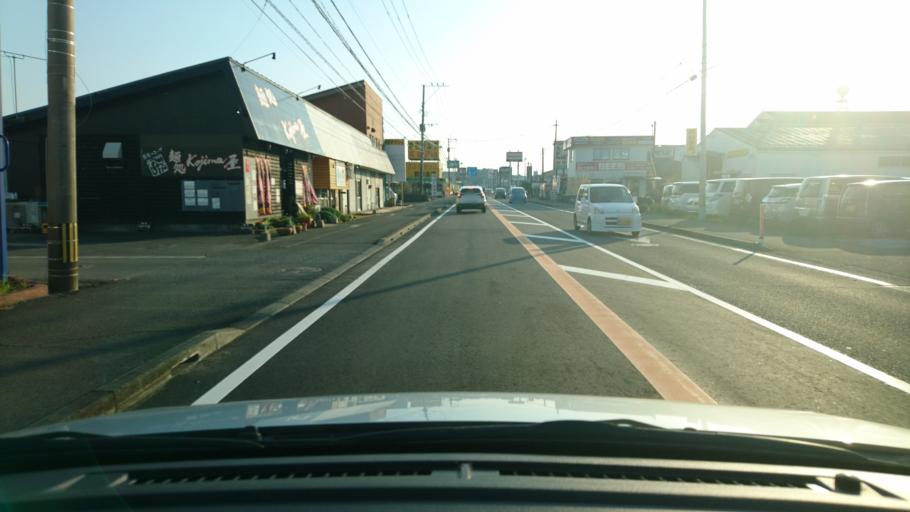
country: JP
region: Miyazaki
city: Miyazaki-shi
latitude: 31.9794
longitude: 131.4453
